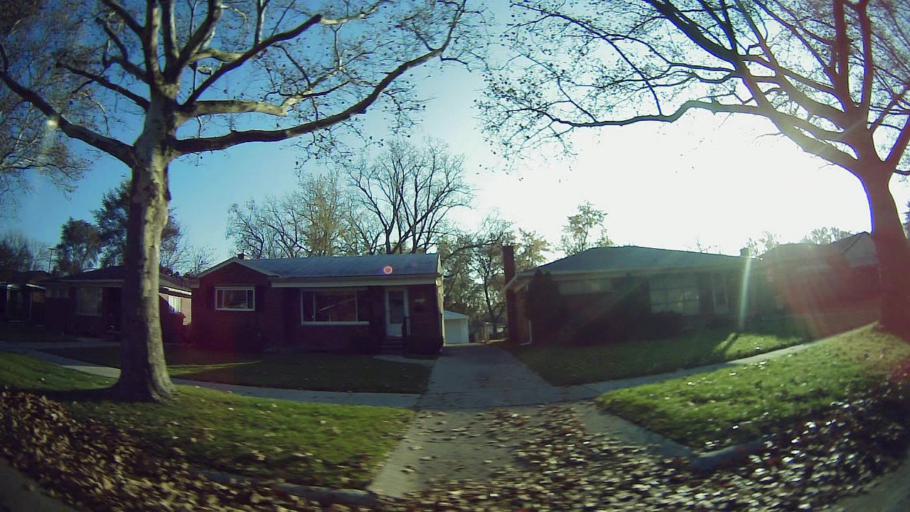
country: US
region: Michigan
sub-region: Oakland County
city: Huntington Woods
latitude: 42.4729
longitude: -83.1628
